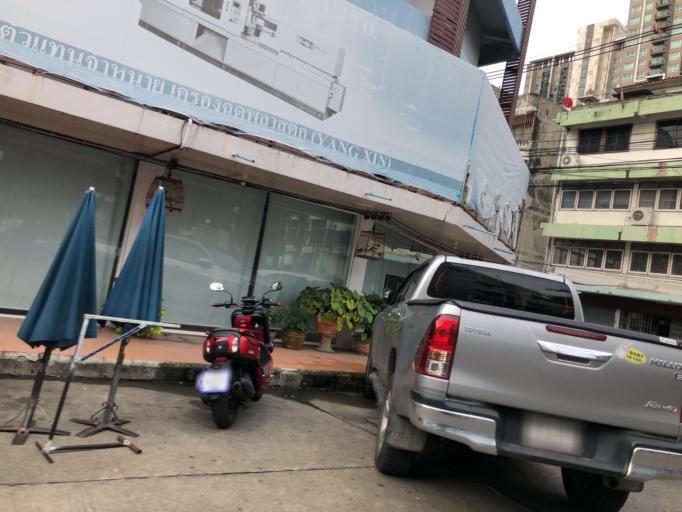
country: TH
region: Bangkok
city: Sathon
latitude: 13.7076
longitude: 100.5316
